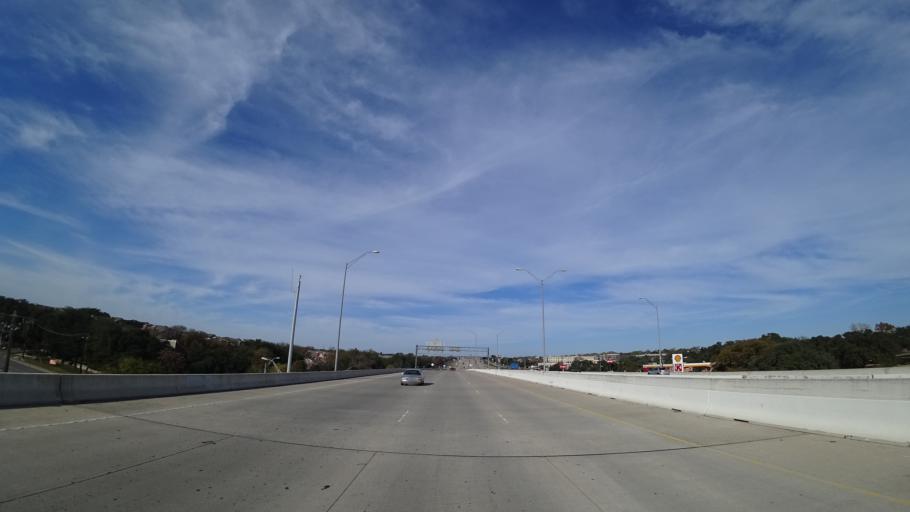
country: US
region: Texas
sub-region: Travis County
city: Austin
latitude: 30.3323
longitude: -97.6860
